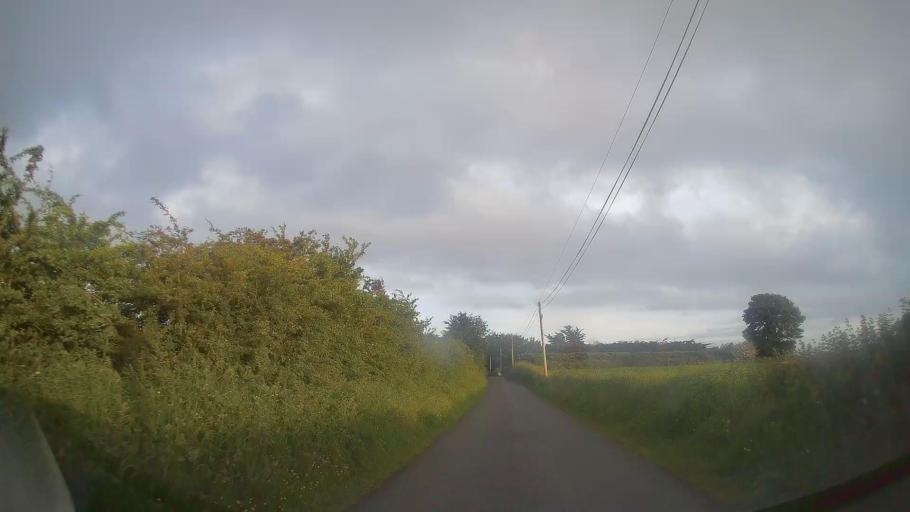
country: IE
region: Munster
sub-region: County Cork
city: Blarney
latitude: 51.9698
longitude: -8.5519
